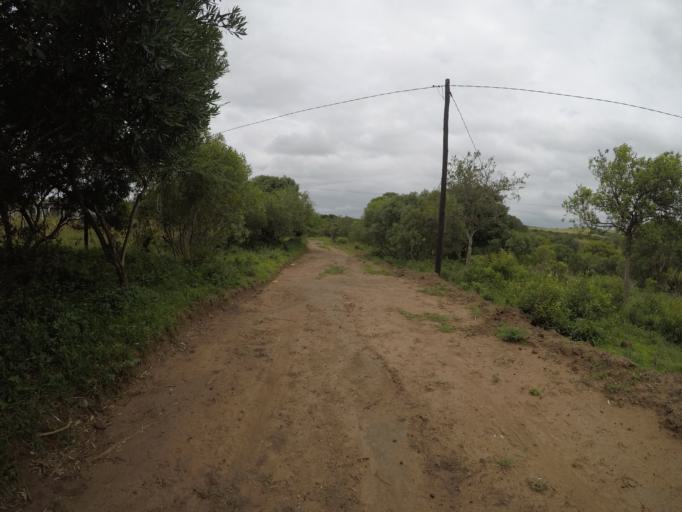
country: ZA
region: KwaZulu-Natal
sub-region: uThungulu District Municipality
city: Empangeni
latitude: -28.6027
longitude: 31.8287
